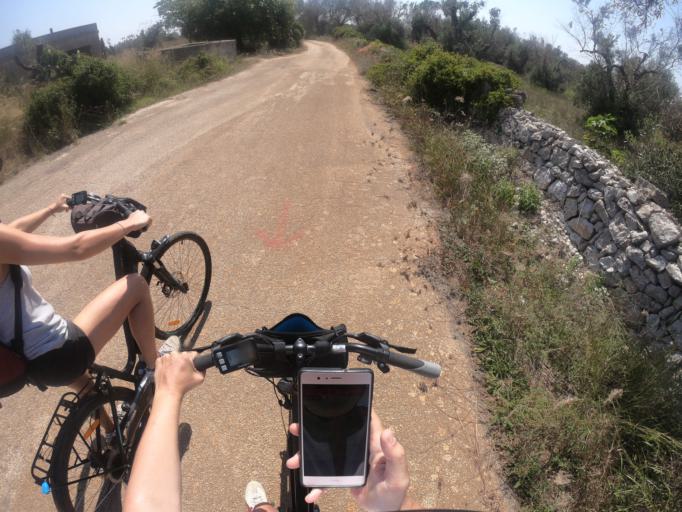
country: IT
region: Apulia
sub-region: Provincia di Lecce
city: Specchia
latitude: 39.9283
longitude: 18.2754
